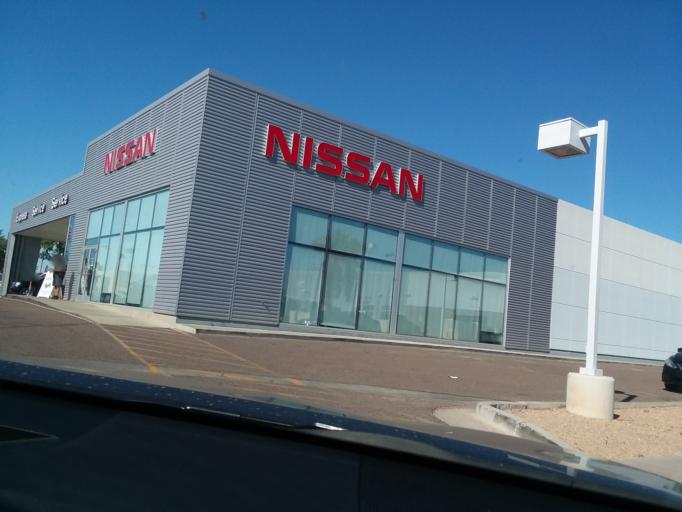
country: US
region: Arizona
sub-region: Maricopa County
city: Phoenix
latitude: 33.5099
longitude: -112.0537
